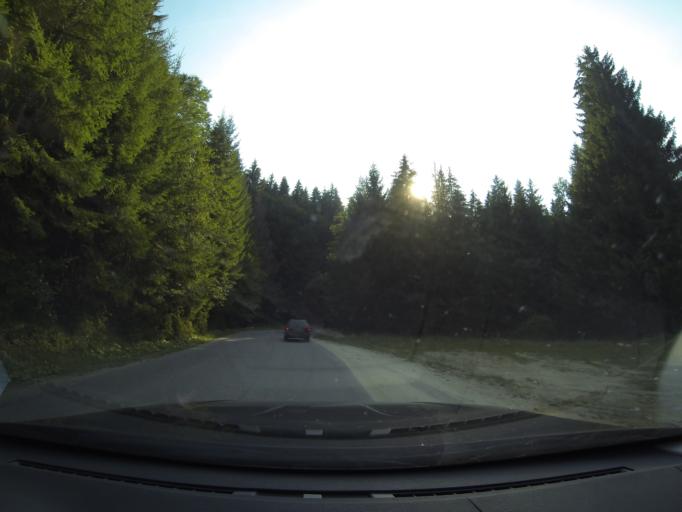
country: RO
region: Arges
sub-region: Comuna Arefu
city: Arefu
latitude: 45.4074
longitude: 24.6377
